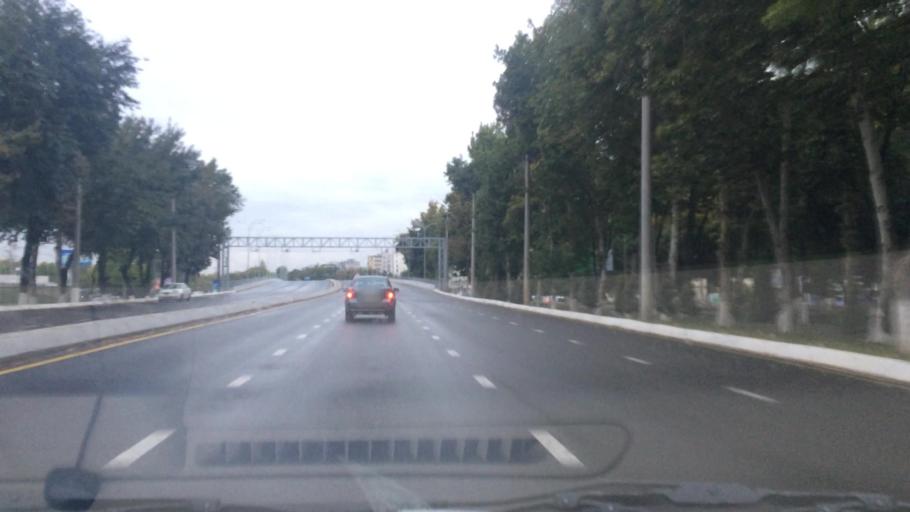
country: UZ
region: Toshkent Shahri
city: Tashkent
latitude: 41.2768
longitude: 69.2066
